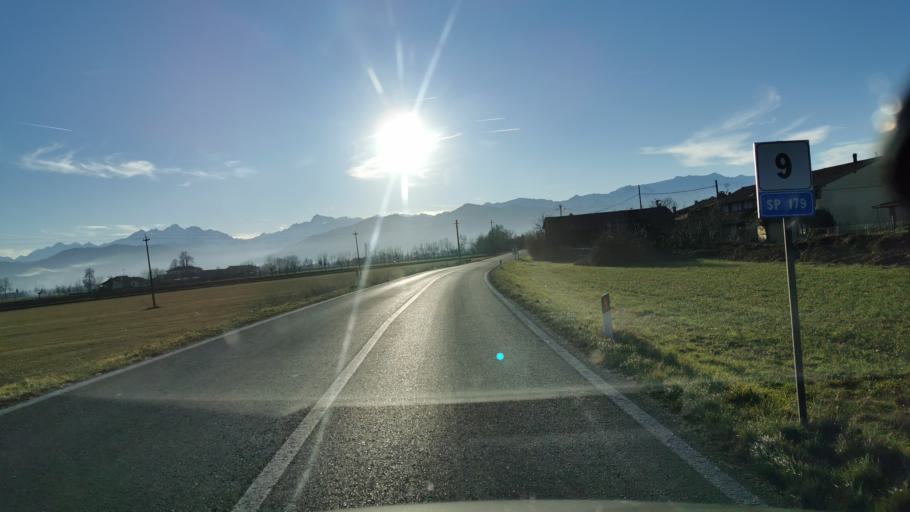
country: IT
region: Piedmont
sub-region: Provincia di Cuneo
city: Roata Rossi
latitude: 44.4544
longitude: 7.4864
